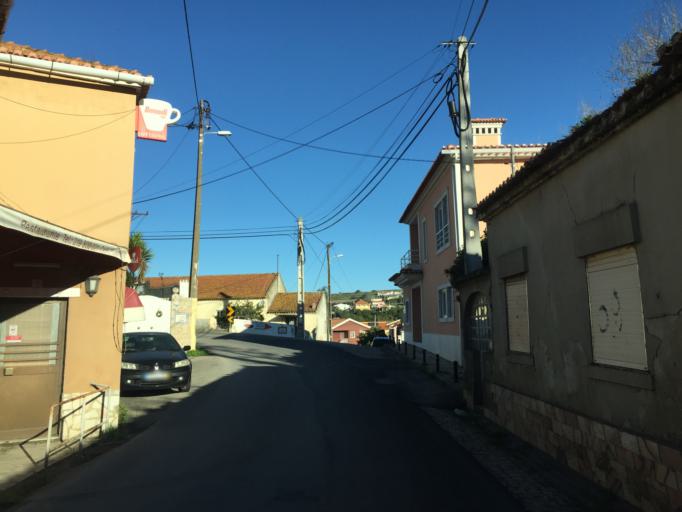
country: PT
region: Lisbon
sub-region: Odivelas
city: Canecas
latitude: 38.8243
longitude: -9.2384
